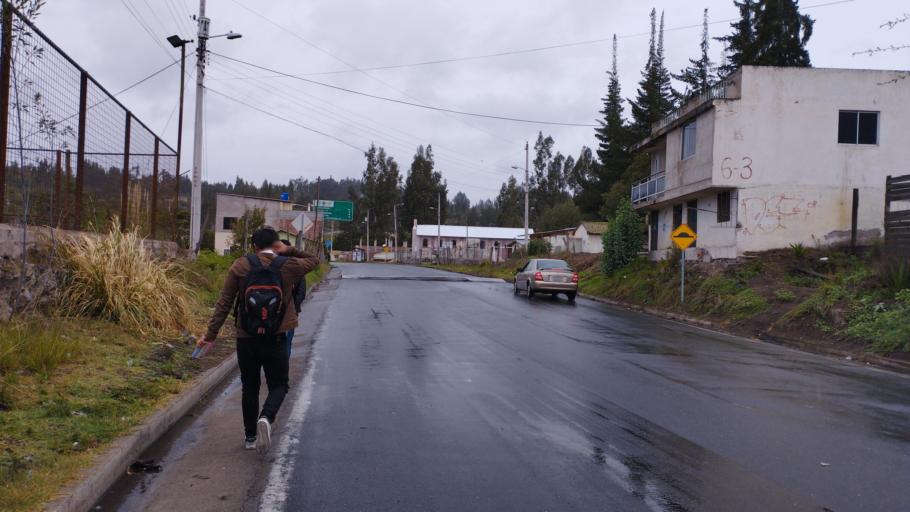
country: EC
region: Chimborazo
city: Guano
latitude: -1.6212
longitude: -78.6107
